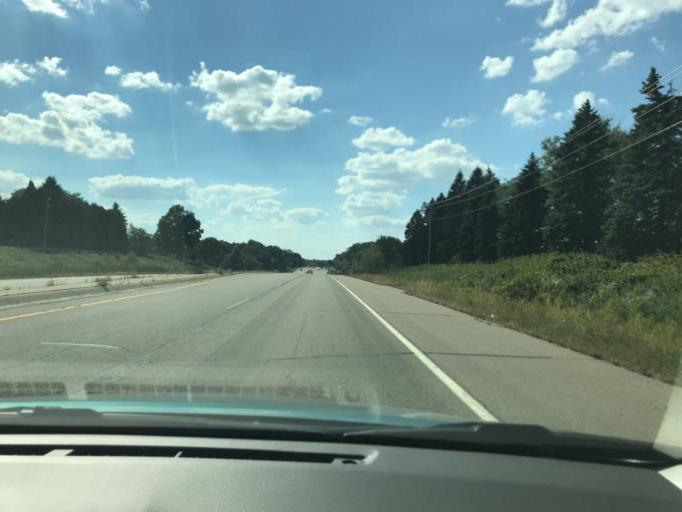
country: US
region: Wisconsin
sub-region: Walworth County
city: Como
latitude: 42.5861
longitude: -88.4849
